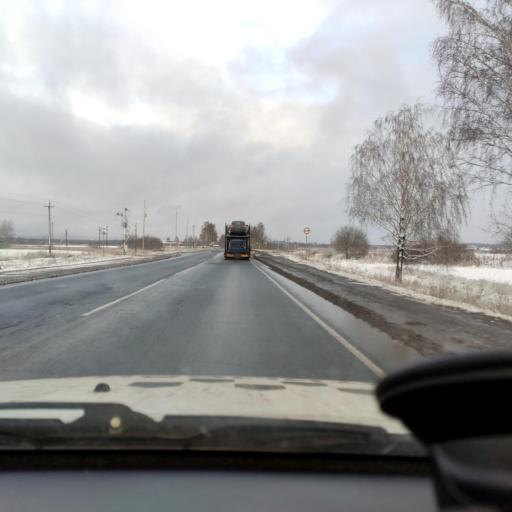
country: RU
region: Perm
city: Ust'-Kachka
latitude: 58.0671
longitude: 55.6251
